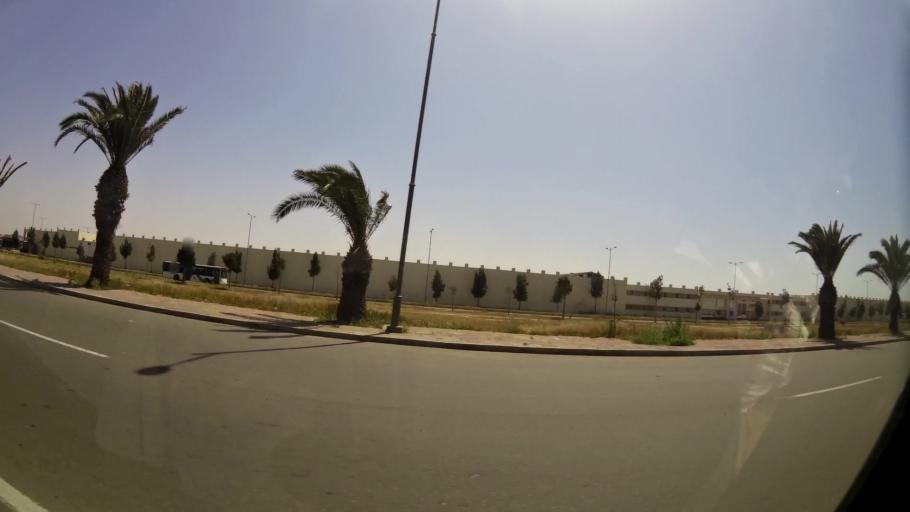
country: MA
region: Souss-Massa-Draa
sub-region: Inezgane-Ait Mellou
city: Inezgane
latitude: 30.3579
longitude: -9.5200
